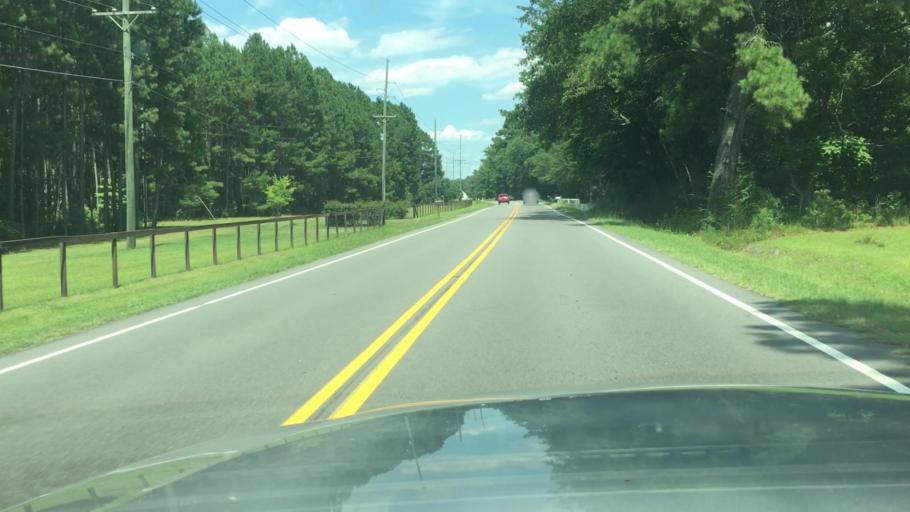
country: US
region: North Carolina
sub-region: Cumberland County
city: Hope Mills
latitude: 34.9473
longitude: -78.8665
